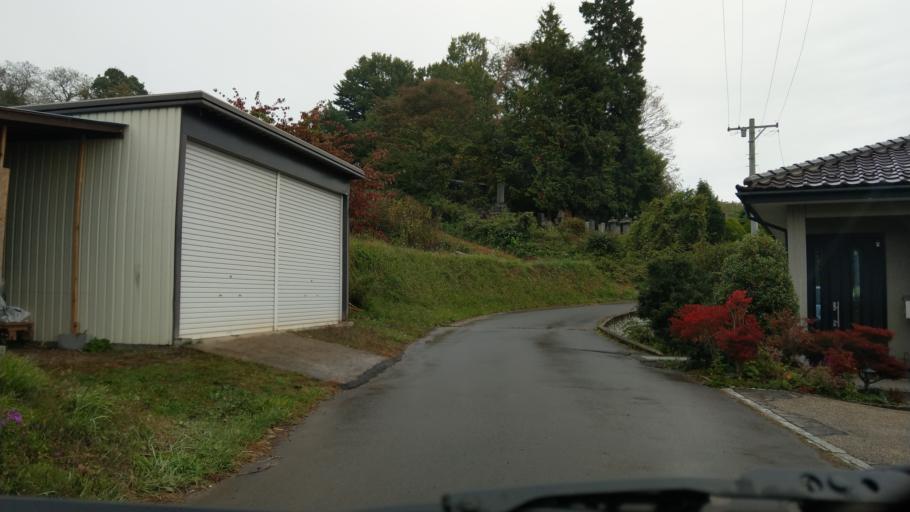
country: JP
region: Nagano
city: Komoro
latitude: 36.3536
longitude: 138.4189
